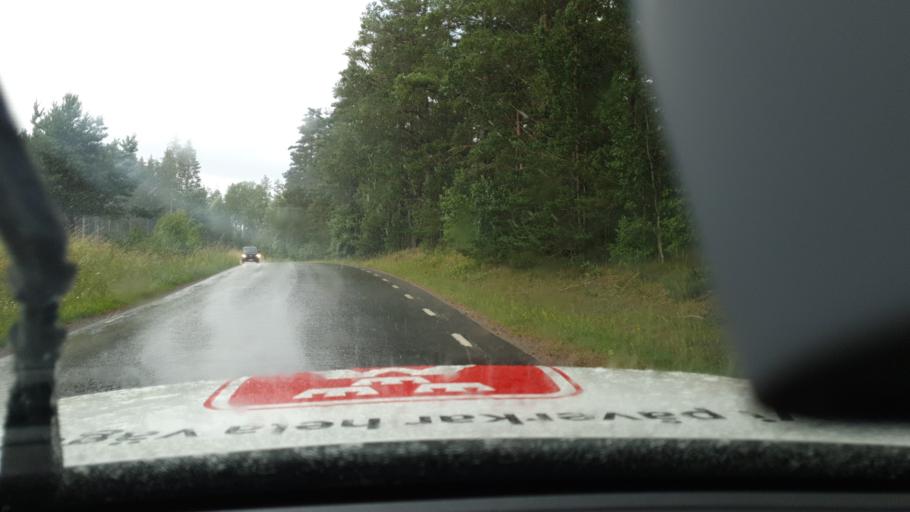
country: SE
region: Vaestra Goetaland
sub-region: Falkopings Kommun
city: Akarp
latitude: 58.2430
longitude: 13.6016
